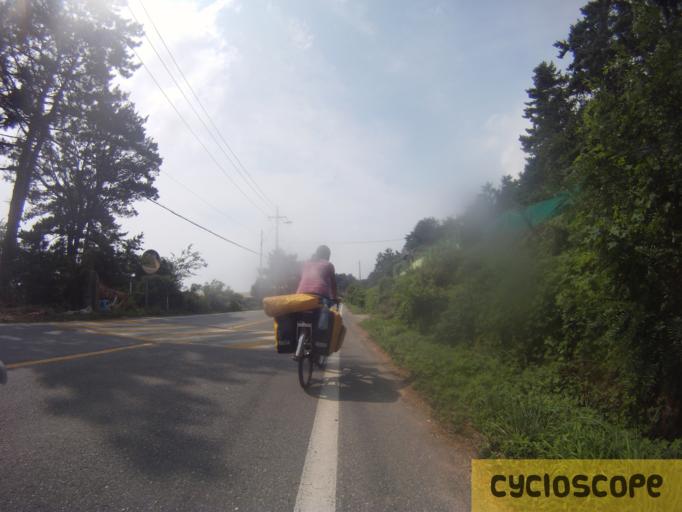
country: KR
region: Busan
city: Kijang
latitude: 35.3109
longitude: 129.2605
